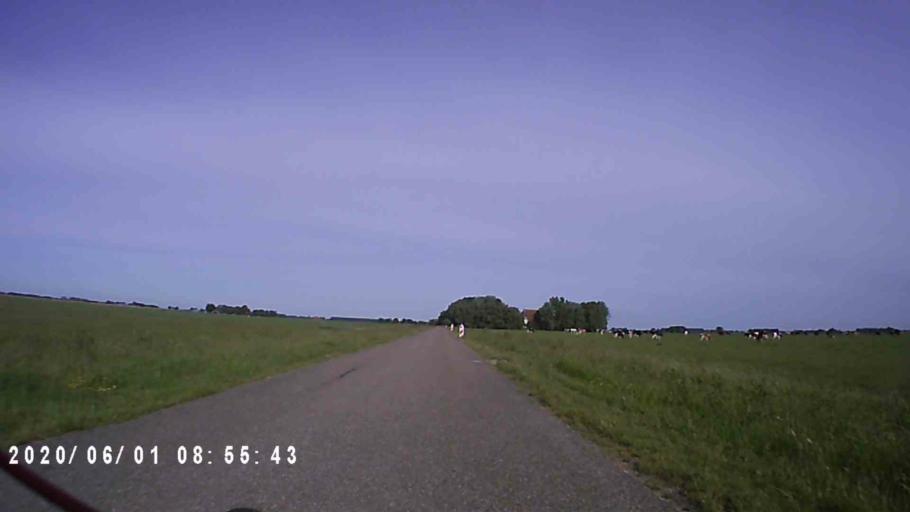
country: NL
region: Friesland
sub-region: Gemeente Leeuwarderadeel
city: Britsum
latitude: 53.2787
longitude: 5.8229
